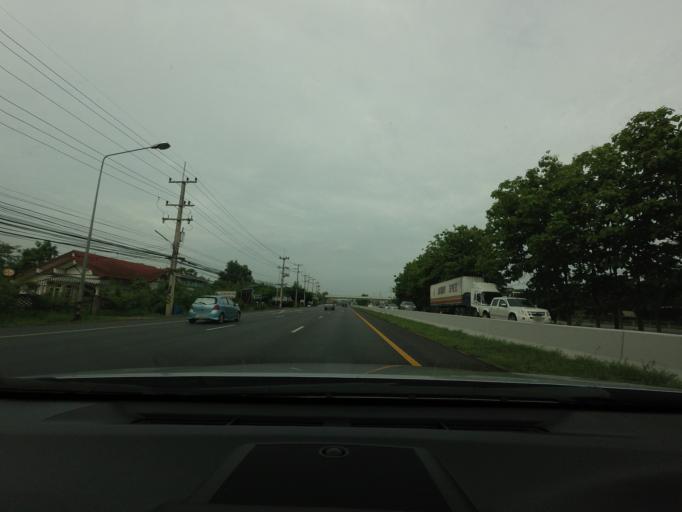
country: TH
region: Phetchaburi
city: Phetchaburi
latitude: 13.1214
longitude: 99.8936
